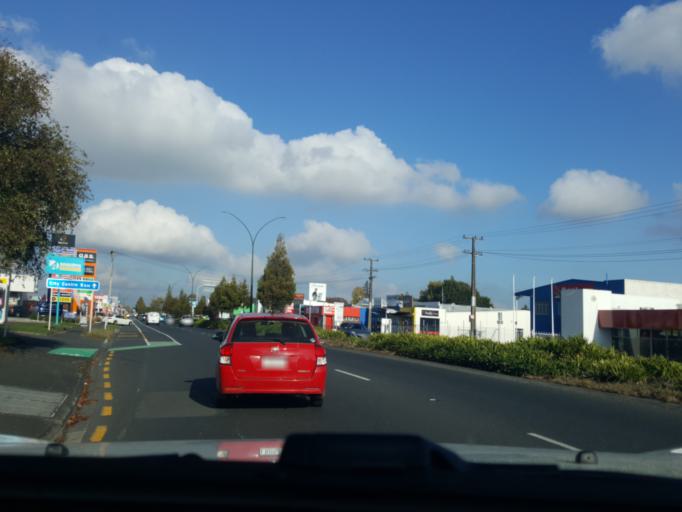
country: NZ
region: Waikato
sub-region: Hamilton City
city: Hamilton
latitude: -37.7579
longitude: 175.2465
